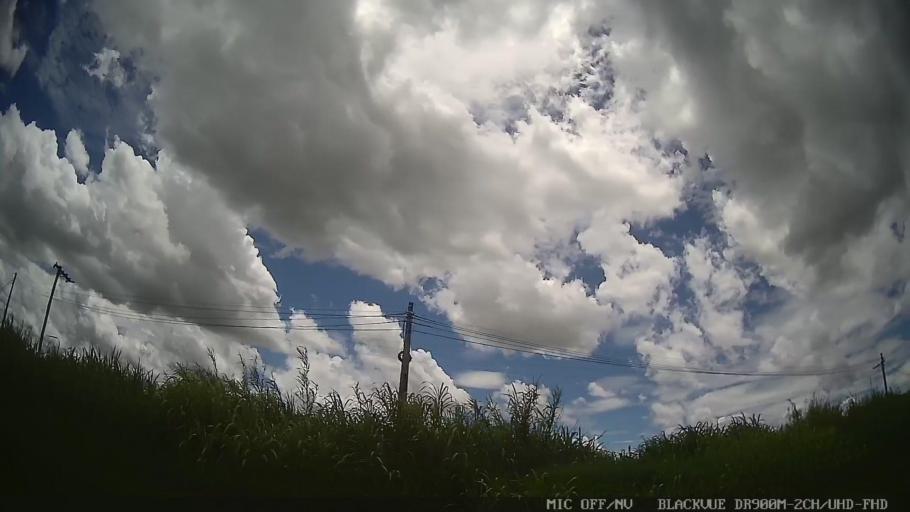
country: BR
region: Sao Paulo
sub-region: Pedreira
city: Pedreira
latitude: -22.7206
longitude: -46.9333
